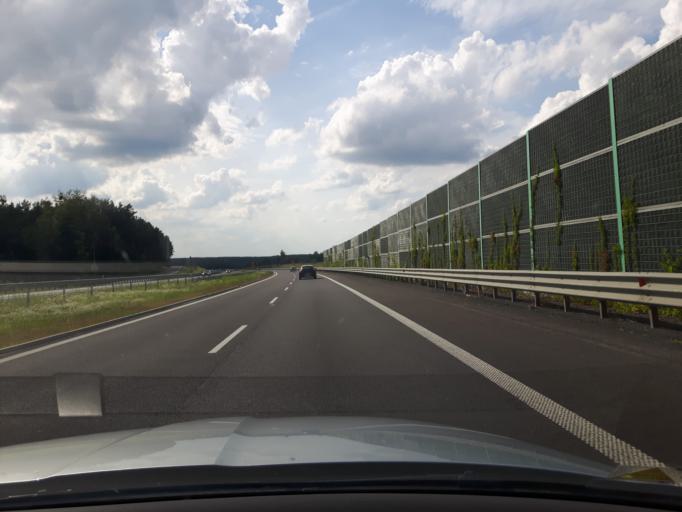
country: PL
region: Warmian-Masurian Voivodeship
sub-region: Powiat olsztynski
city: Olsztynek
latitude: 53.5869
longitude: 20.2427
